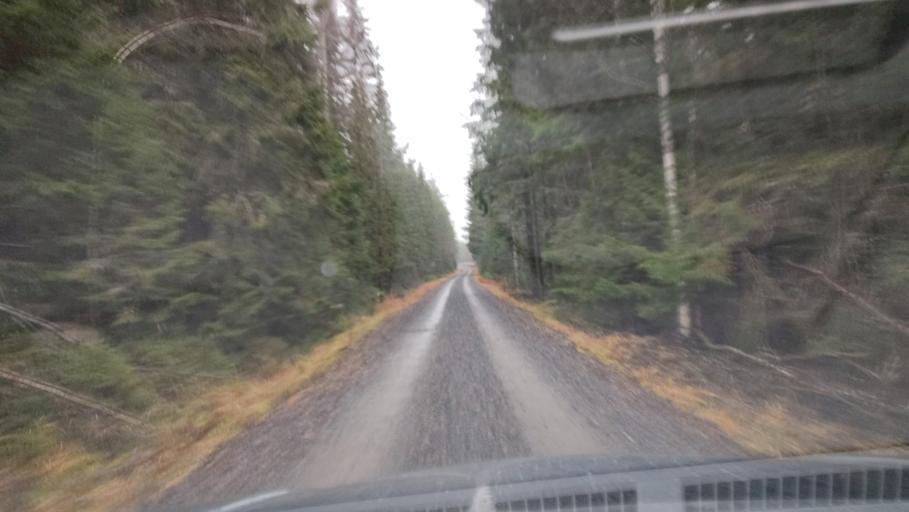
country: FI
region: Southern Ostrobothnia
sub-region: Suupohja
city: Karijoki
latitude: 62.1411
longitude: 21.6273
